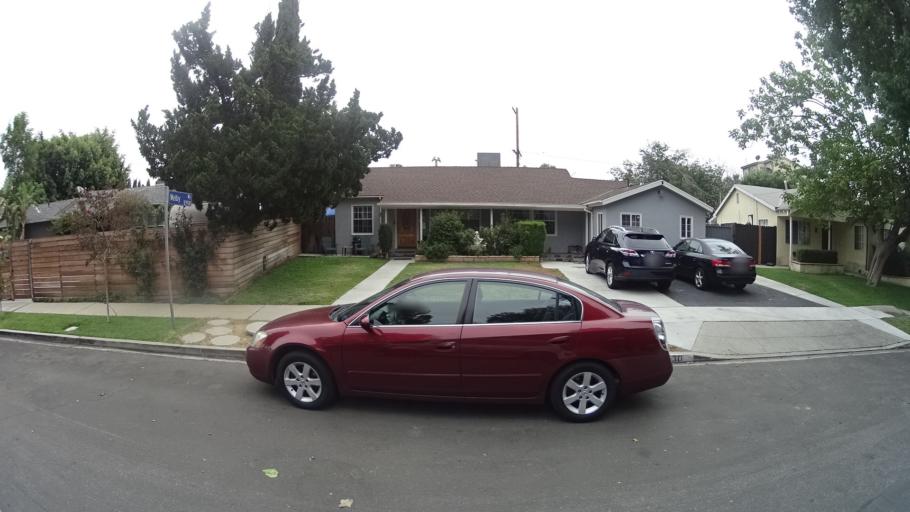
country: US
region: California
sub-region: Los Angeles County
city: Van Nuys
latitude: 34.1930
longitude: -118.4148
